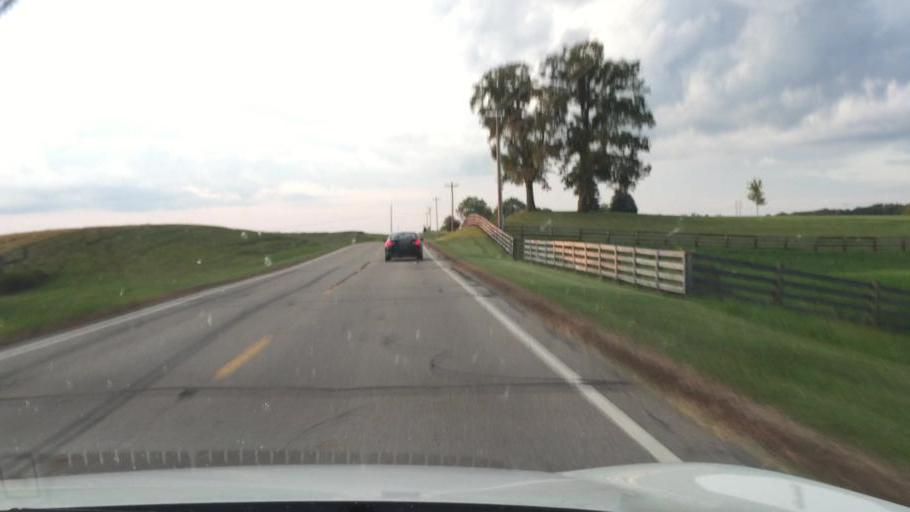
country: US
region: Ohio
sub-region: Champaign County
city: Mechanicsburg
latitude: 40.0508
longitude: -83.5681
